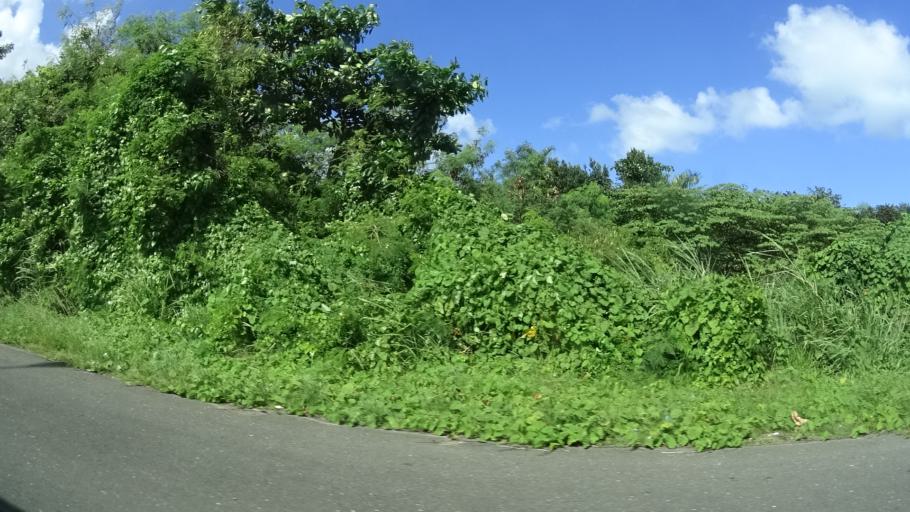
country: PR
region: Luquillo
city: Playa Fortuna
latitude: 18.3794
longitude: -65.7491
